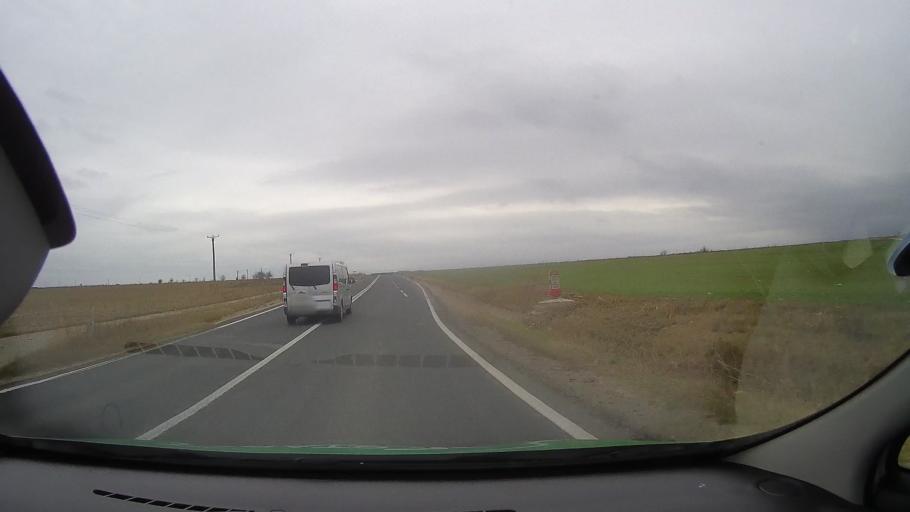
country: RO
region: Constanta
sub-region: Comuna Nicolae Balcescu
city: Nicolae Balcescu
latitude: 44.3831
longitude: 28.3996
